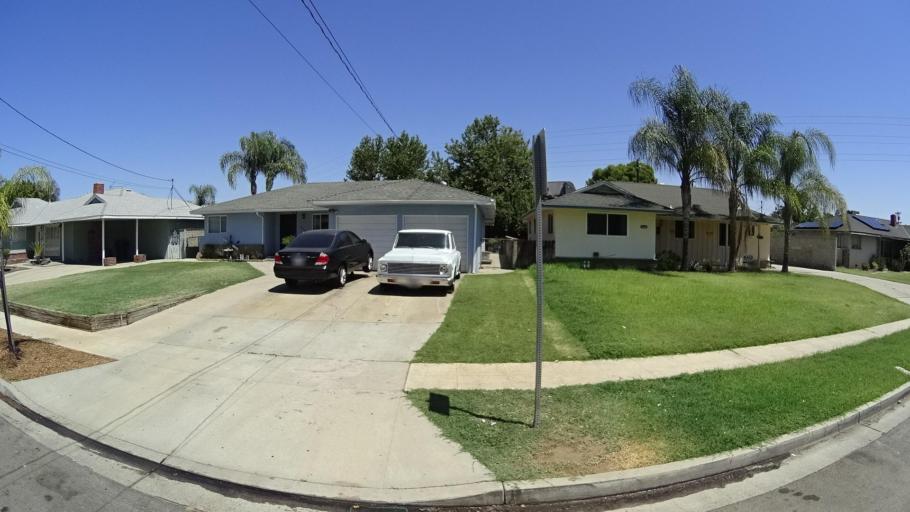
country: US
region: California
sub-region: Fresno County
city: Fresno
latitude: 36.7686
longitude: -119.7437
